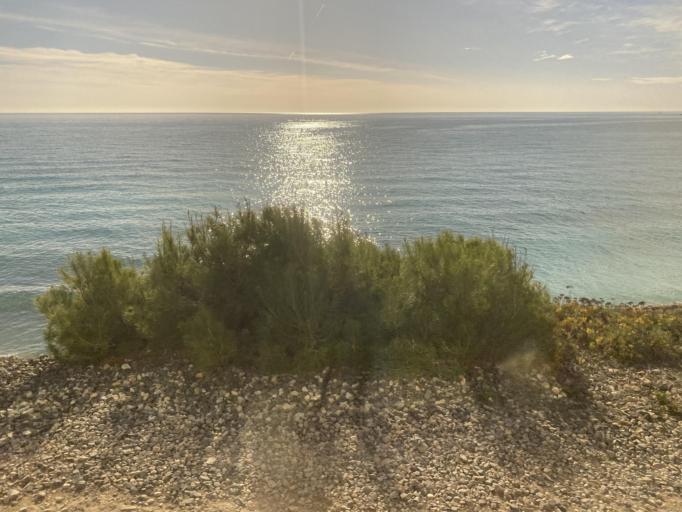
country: ES
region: Catalonia
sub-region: Provincia de Barcelona
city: Vilanova i la Geltru
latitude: 41.2200
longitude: 1.7537
